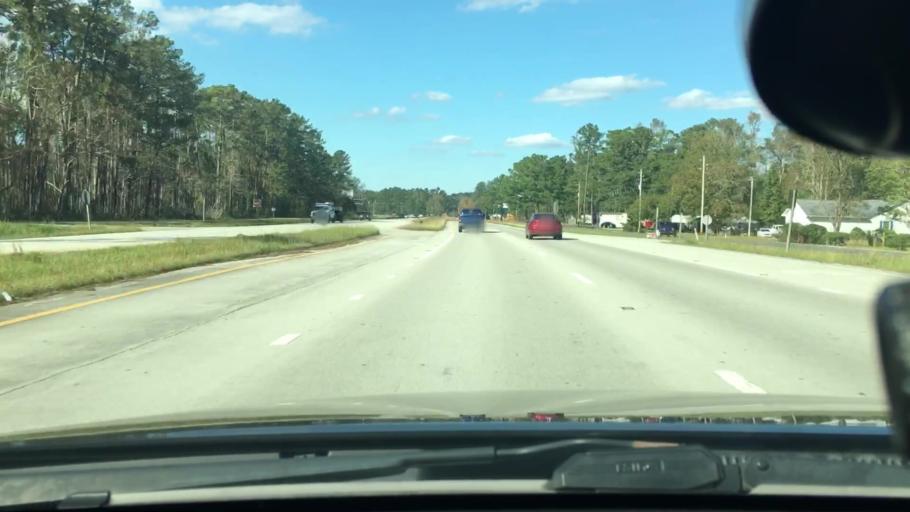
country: US
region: North Carolina
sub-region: Craven County
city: Neuse Forest
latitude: 34.9471
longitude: -76.9483
